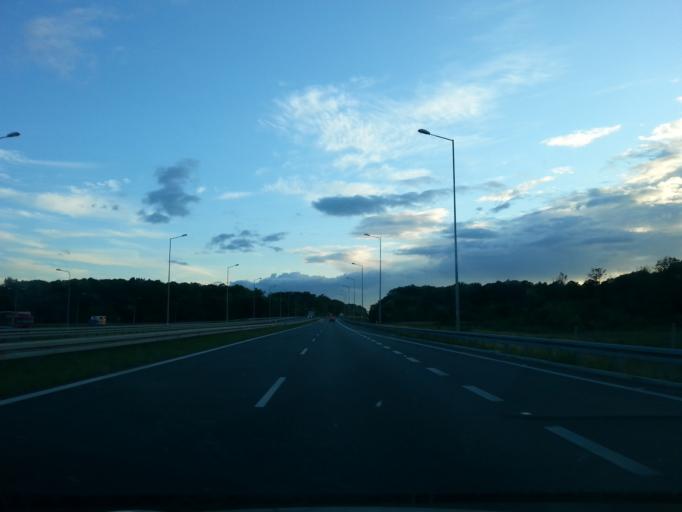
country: PL
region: Lower Silesian Voivodeship
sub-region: Powiat olesnicki
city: Sycow
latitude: 51.2952
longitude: 17.7350
